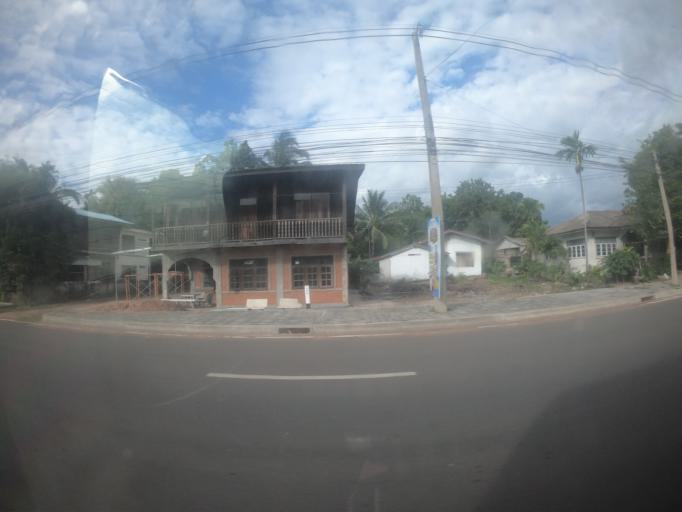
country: TH
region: Surin
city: Prasat
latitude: 14.6168
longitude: 103.4155
